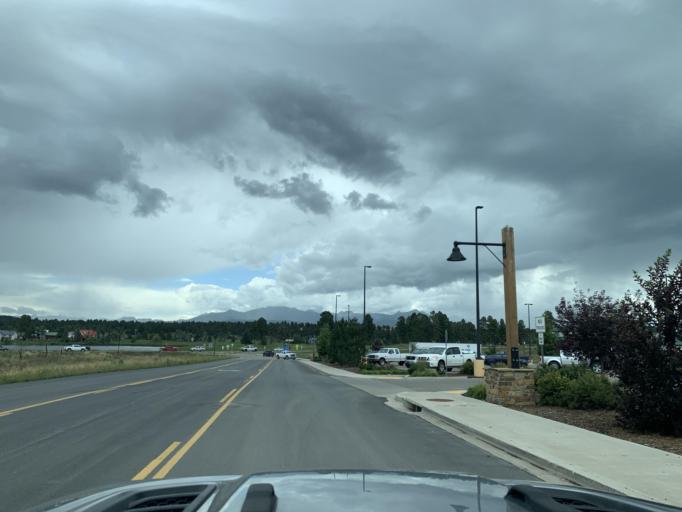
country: US
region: Colorado
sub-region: Archuleta County
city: Pagosa Springs
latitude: 37.2598
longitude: -107.0643
